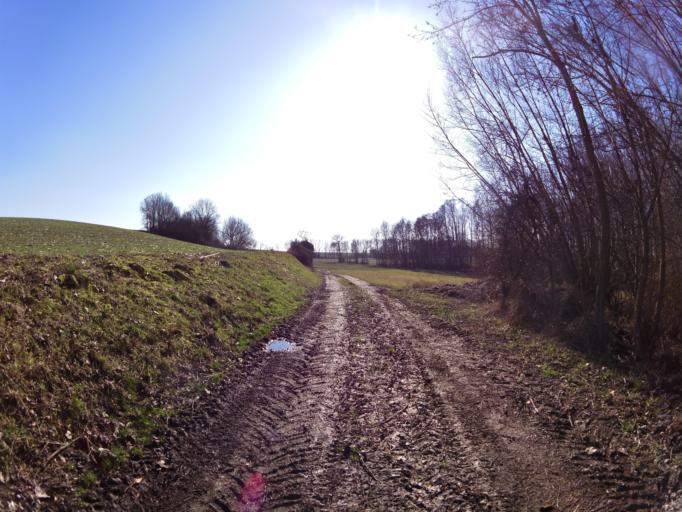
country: DE
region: Bavaria
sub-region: Regierungsbezirk Unterfranken
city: Giebelstadt
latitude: 49.6939
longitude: 9.9648
